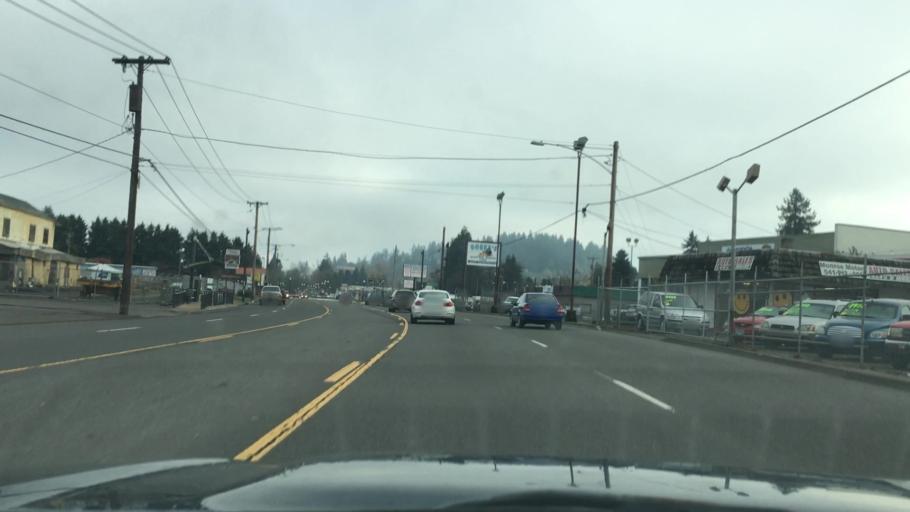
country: US
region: Oregon
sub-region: Lane County
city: Springfield
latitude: 44.0450
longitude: -123.0372
